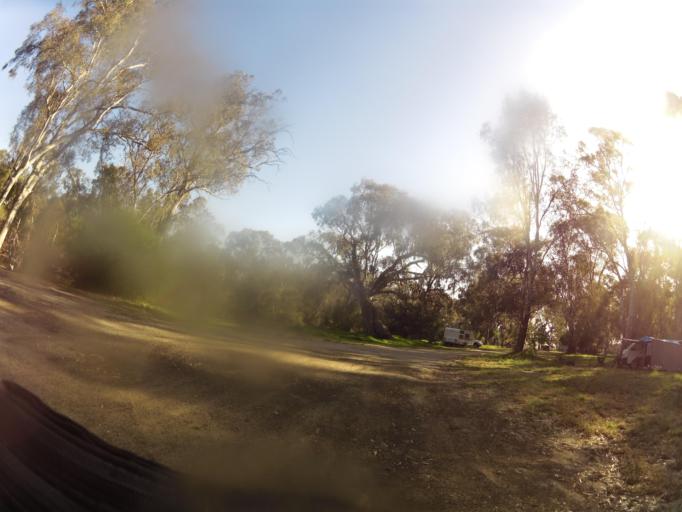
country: AU
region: Victoria
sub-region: Murrindindi
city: Kinglake West
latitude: -37.0193
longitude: 145.1157
